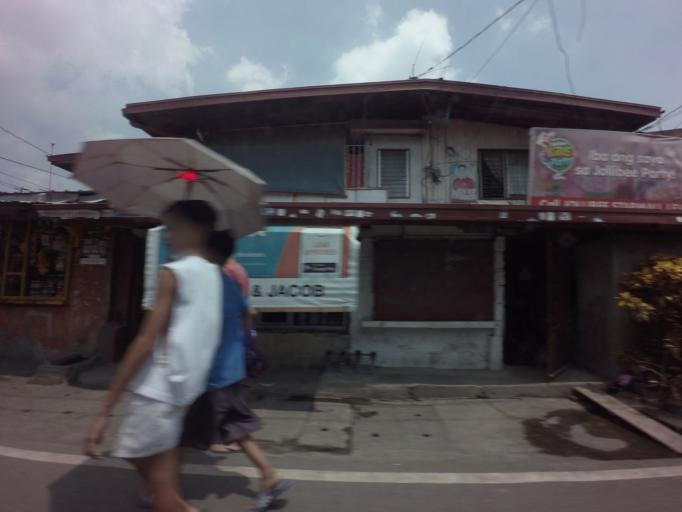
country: PH
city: Sambayanihan People's Village
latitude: 14.4378
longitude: 121.0503
